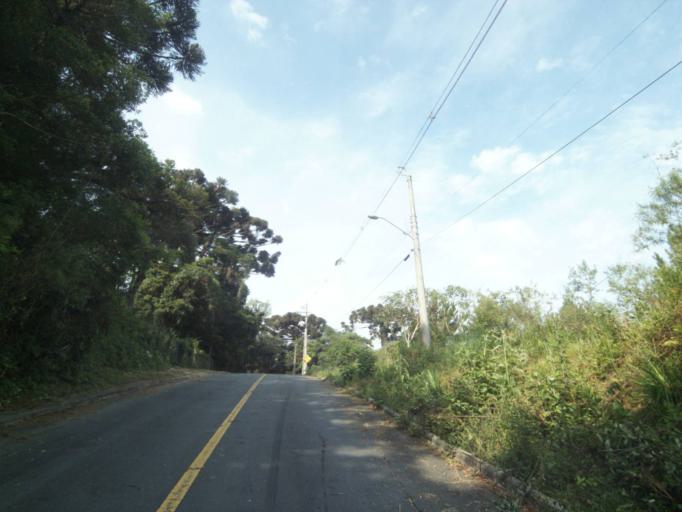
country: BR
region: Parana
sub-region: Curitiba
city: Curitiba
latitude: -25.4123
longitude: -49.3181
